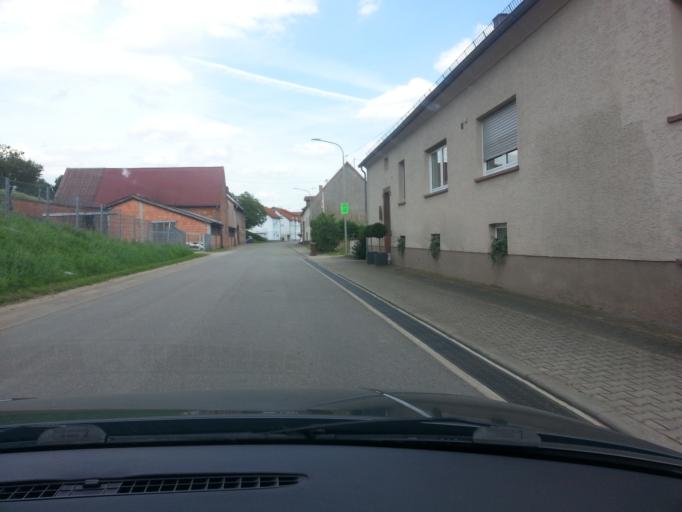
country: DE
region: Rheinland-Pfalz
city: Mauschbach
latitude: 49.1859
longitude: 7.3865
